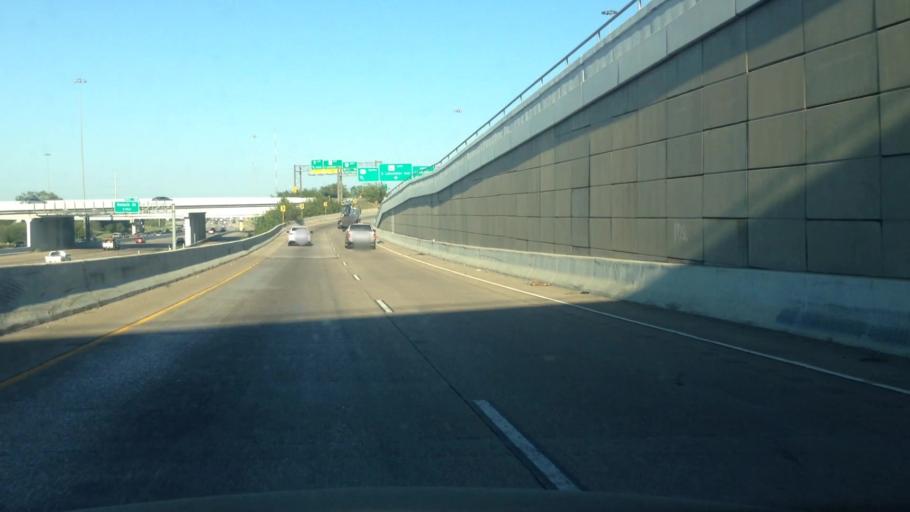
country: US
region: Texas
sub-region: Tarrant County
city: Fort Worth
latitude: 32.7470
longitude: -97.3118
